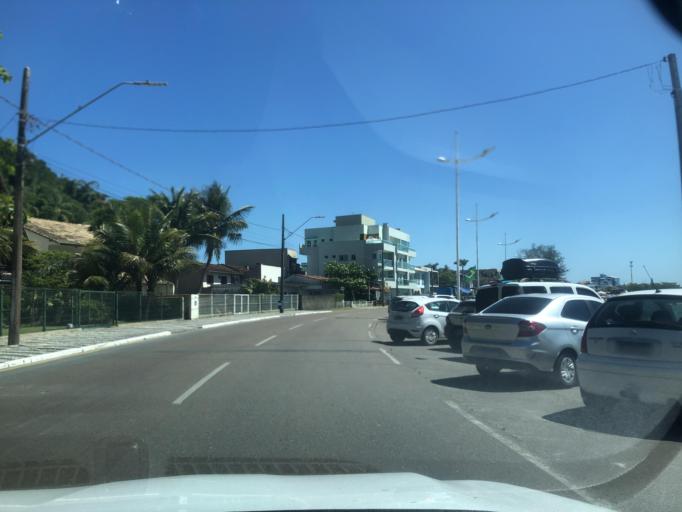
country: BR
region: Santa Catarina
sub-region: Sao Francisco Do Sul
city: Sao Francisco do Sul
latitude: -26.2230
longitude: -48.5010
